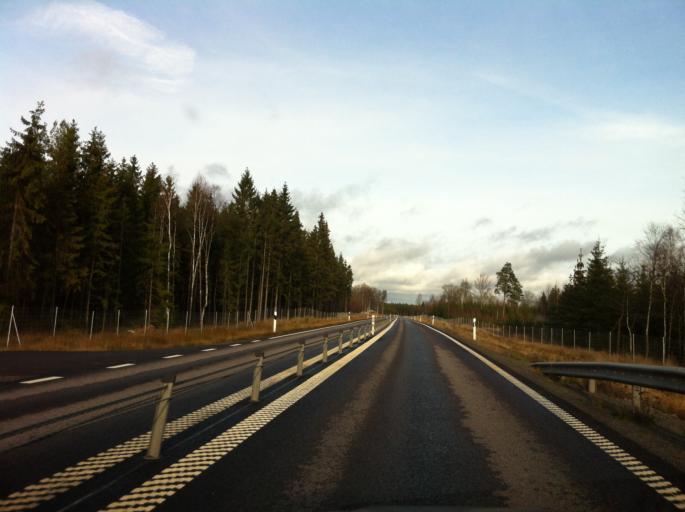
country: SE
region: Kronoberg
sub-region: Almhults Kommun
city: AElmhult
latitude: 56.6373
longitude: 14.2632
